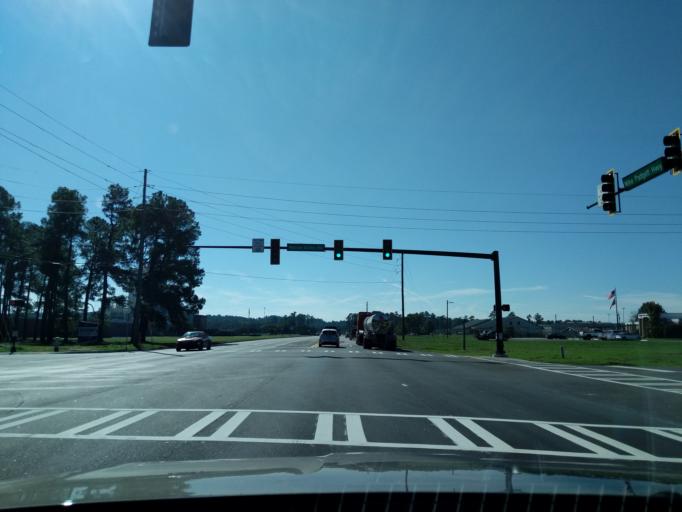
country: US
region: Georgia
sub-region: Richmond County
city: Augusta
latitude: 33.3946
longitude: -82.0053
